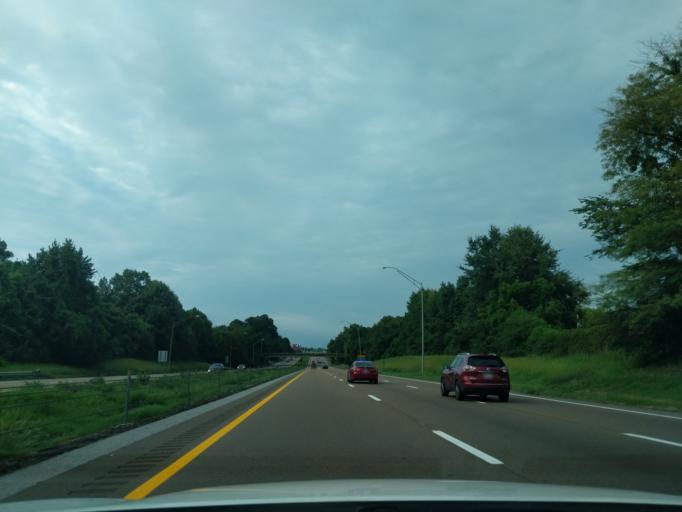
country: US
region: Tennessee
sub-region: Shelby County
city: New South Memphis
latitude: 35.0989
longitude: -90.0763
